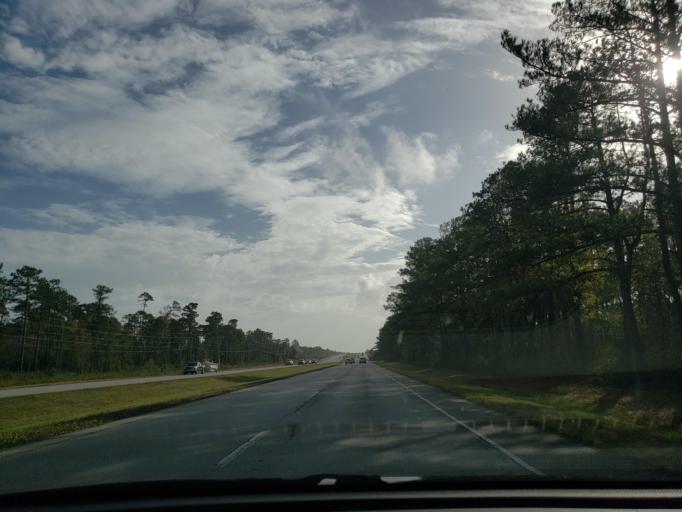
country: US
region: North Carolina
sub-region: Onslow County
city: Jacksonville
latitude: 34.6431
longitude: -77.4784
